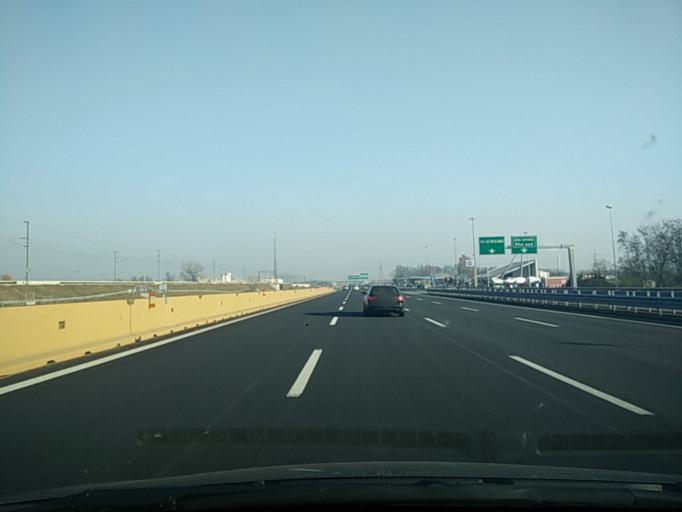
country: IT
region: Lombardy
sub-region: Citta metropolitana di Milano
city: Vighignolo
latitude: 45.5095
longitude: 9.0355
